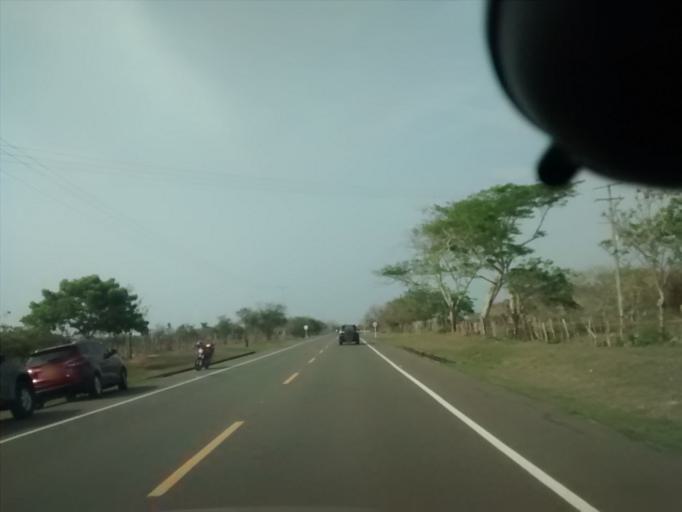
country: CO
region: Bolivar
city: Clemencia
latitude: 10.6329
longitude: -75.4221
